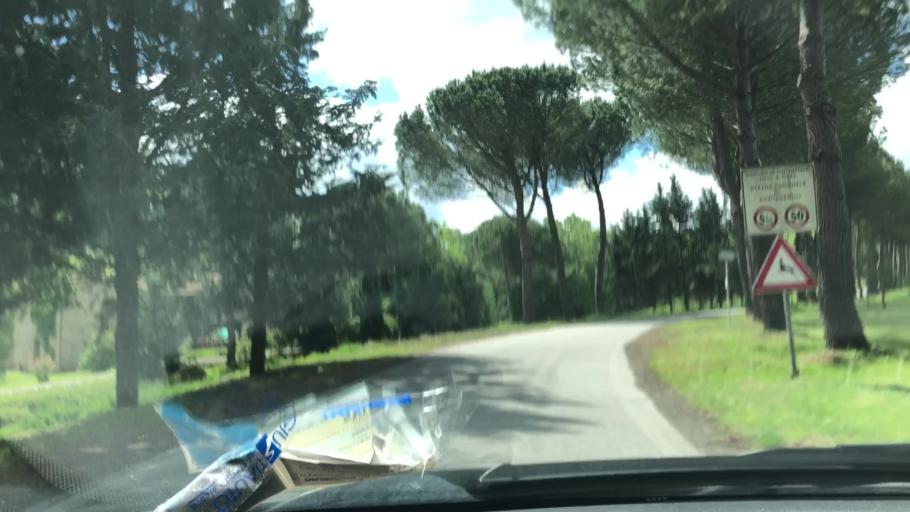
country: IT
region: Tuscany
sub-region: Province of Pisa
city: Saline
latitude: 43.3495
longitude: 10.7928
